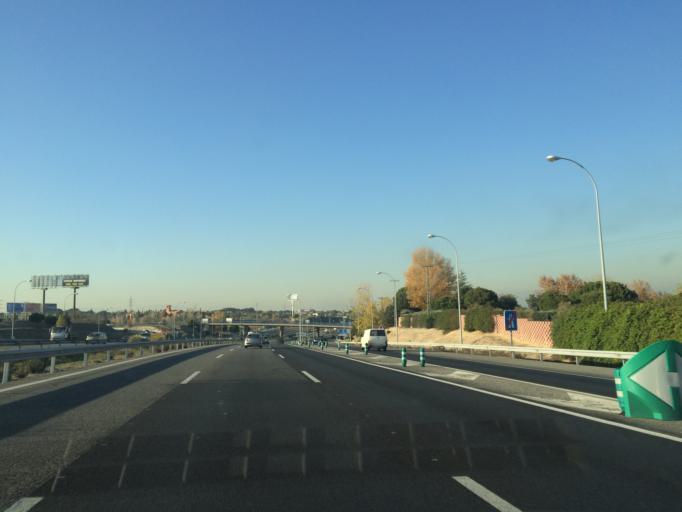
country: ES
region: Madrid
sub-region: Provincia de Madrid
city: Pozuelo de Alarcon
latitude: 40.4225
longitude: -3.8321
